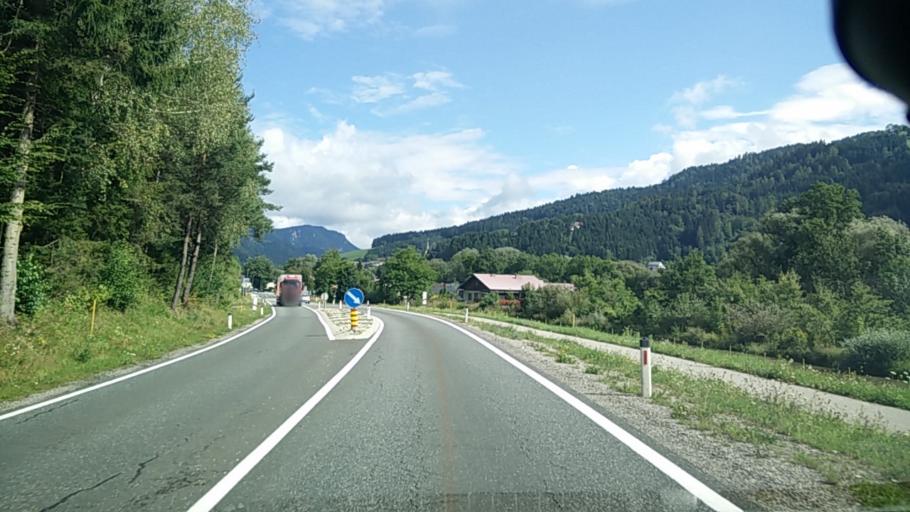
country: AT
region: Carinthia
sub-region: Politischer Bezirk Sankt Veit an der Glan
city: Bruckl
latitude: 46.7428
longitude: 14.5312
